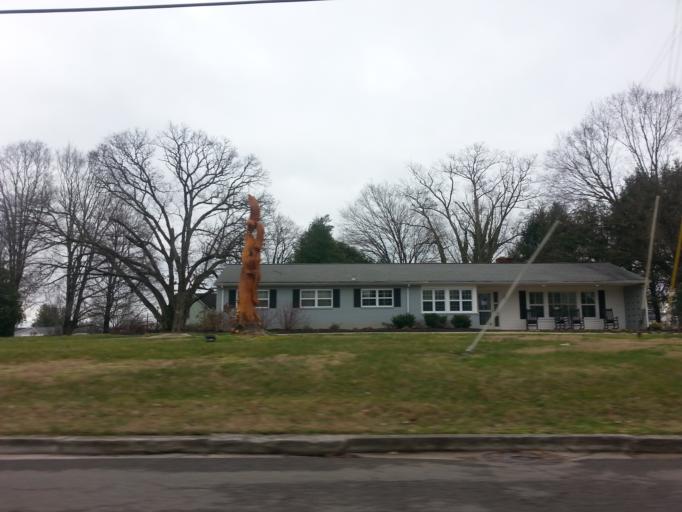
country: US
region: Tennessee
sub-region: Jefferson County
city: Jefferson City
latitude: 36.1190
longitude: -83.4924
